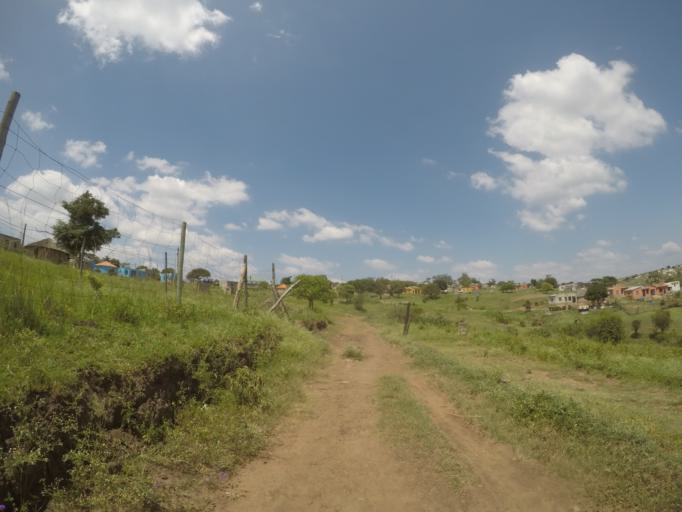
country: ZA
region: KwaZulu-Natal
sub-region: uThungulu District Municipality
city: Empangeni
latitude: -28.6012
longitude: 31.7401
